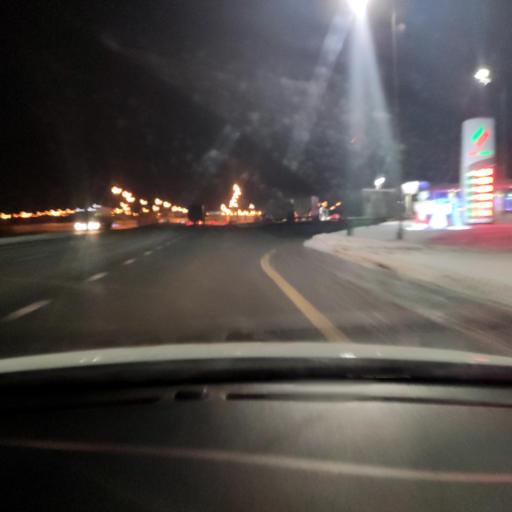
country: RU
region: Tatarstan
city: Vysokaya Gora
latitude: 55.7928
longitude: 49.3391
